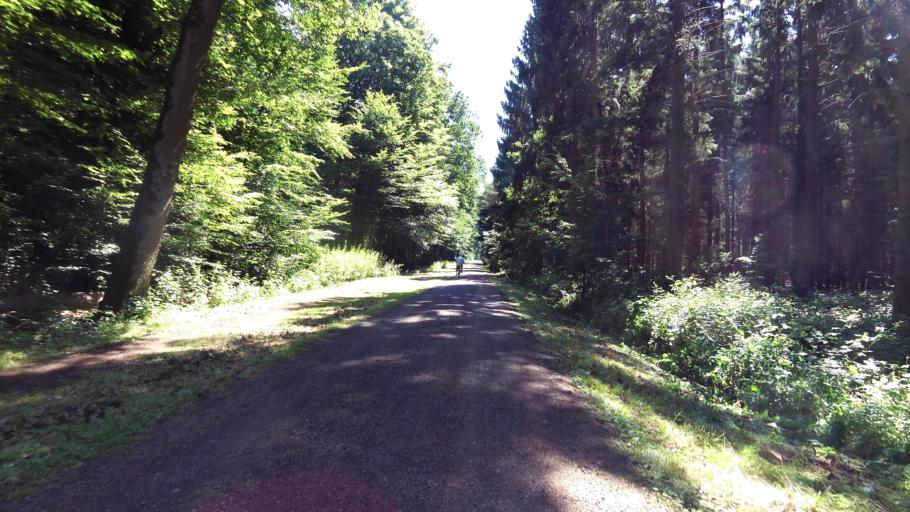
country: DE
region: North Rhine-Westphalia
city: Meckenheim
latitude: 50.6441
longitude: 7.0611
